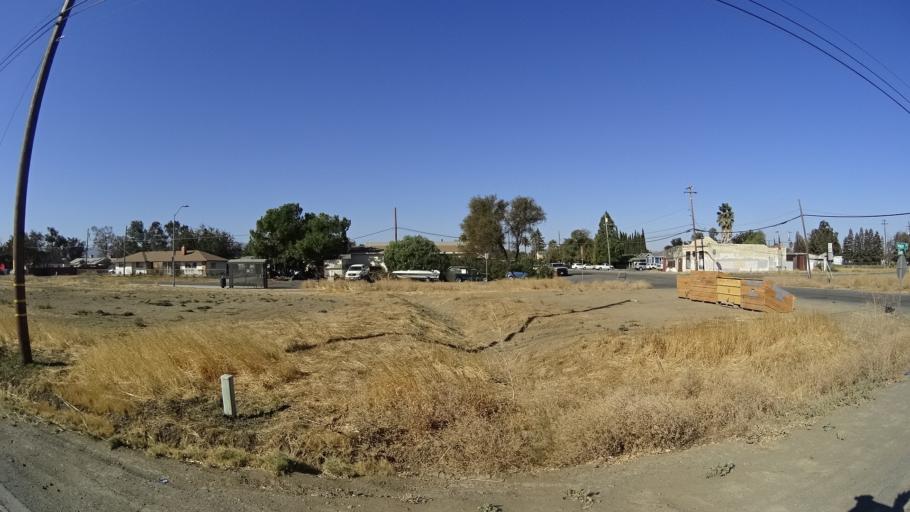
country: US
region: California
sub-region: Yolo County
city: Cottonwood
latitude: 38.6789
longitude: -121.9679
